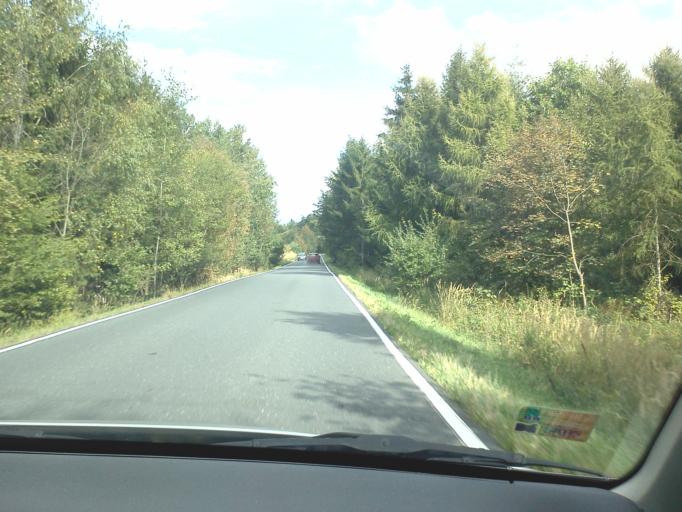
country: CZ
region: Central Bohemia
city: Mukarov
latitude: 50.0017
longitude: 14.7619
